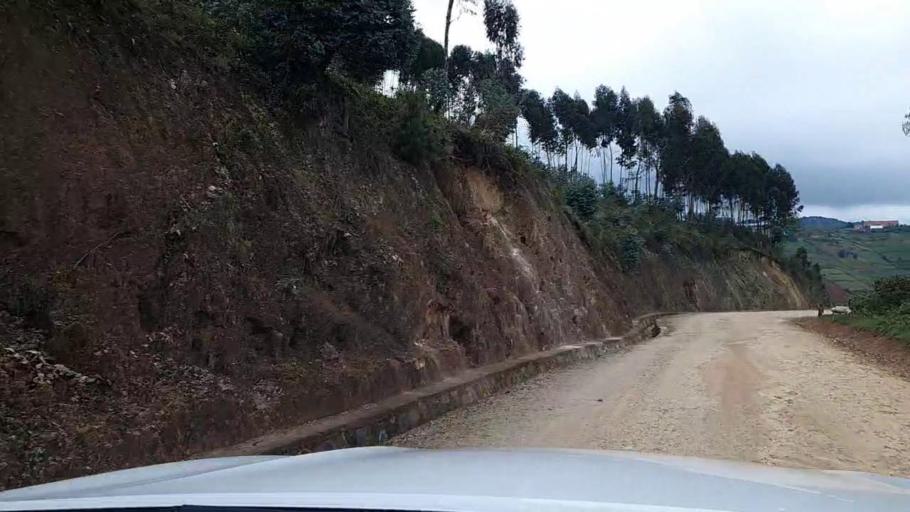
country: RW
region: Southern Province
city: Nzega
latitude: -2.3794
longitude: 29.3828
